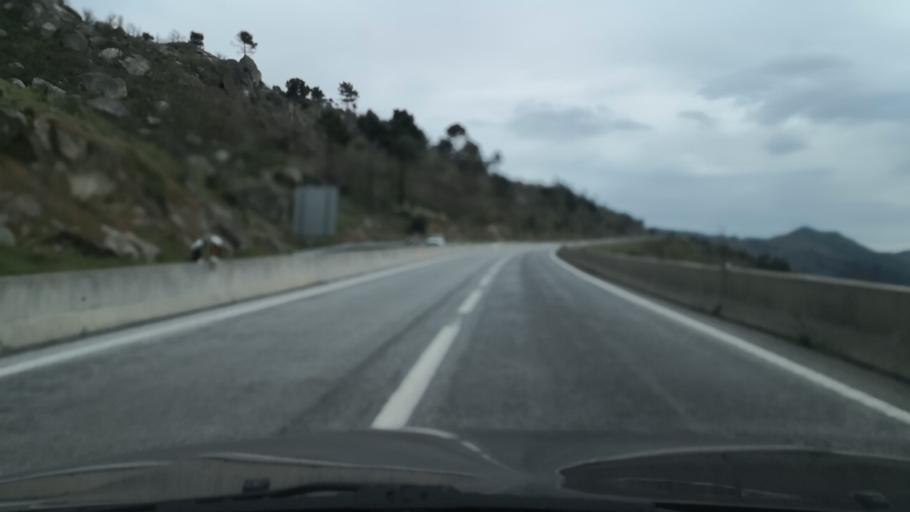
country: PT
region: Guarda
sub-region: Guarda
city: Guarda
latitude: 40.6108
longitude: -7.2834
